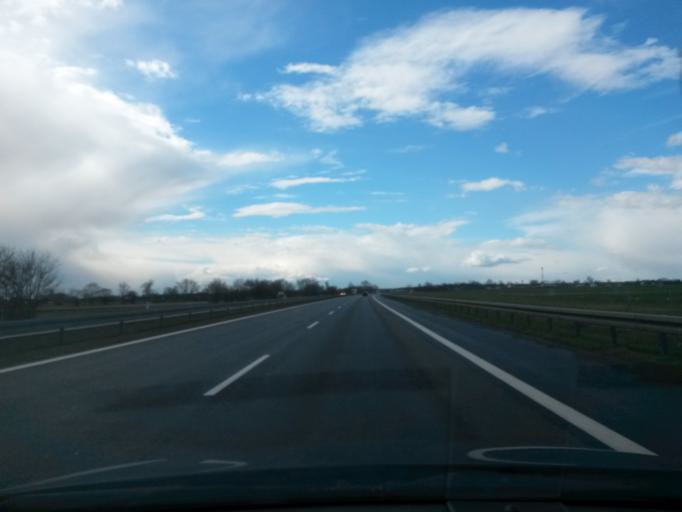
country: PL
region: Greater Poland Voivodeship
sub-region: Powiat slupecki
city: Ladek
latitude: 52.2324
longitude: 17.9036
